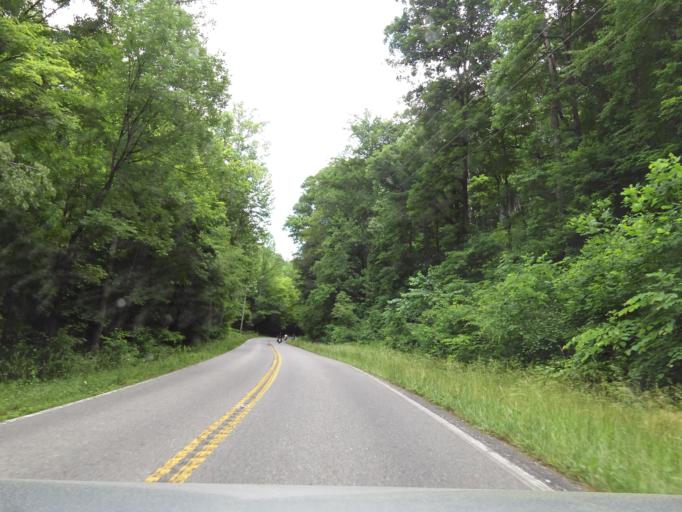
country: US
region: Tennessee
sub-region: Loudon County
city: Greenback
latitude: 35.5633
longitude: -84.0908
